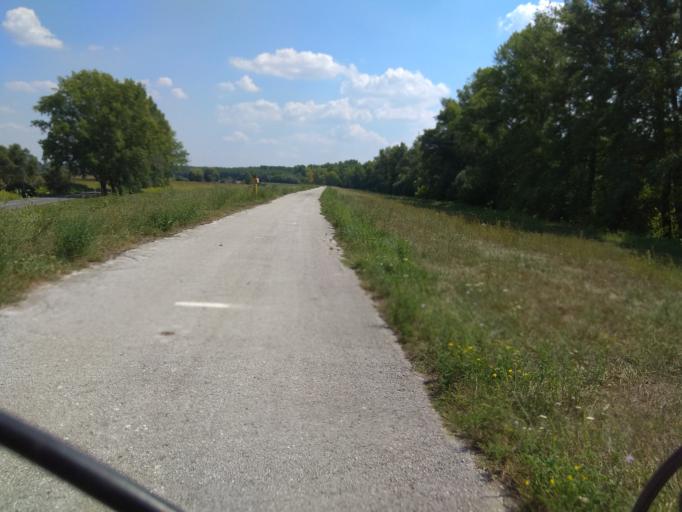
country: SK
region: Trnavsky
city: Gabcikovo
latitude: 47.8152
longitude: 17.6275
